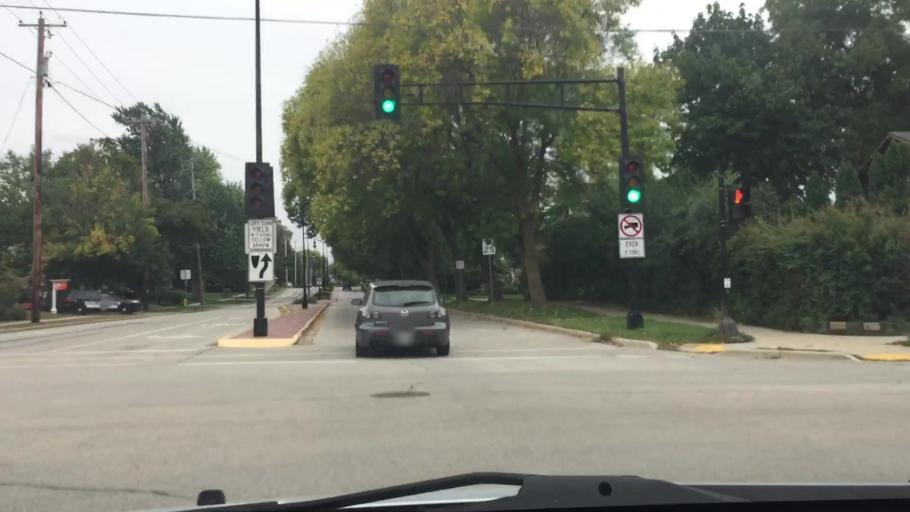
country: US
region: Wisconsin
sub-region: Waukesha County
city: Waukesha
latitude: 43.0029
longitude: -88.2319
